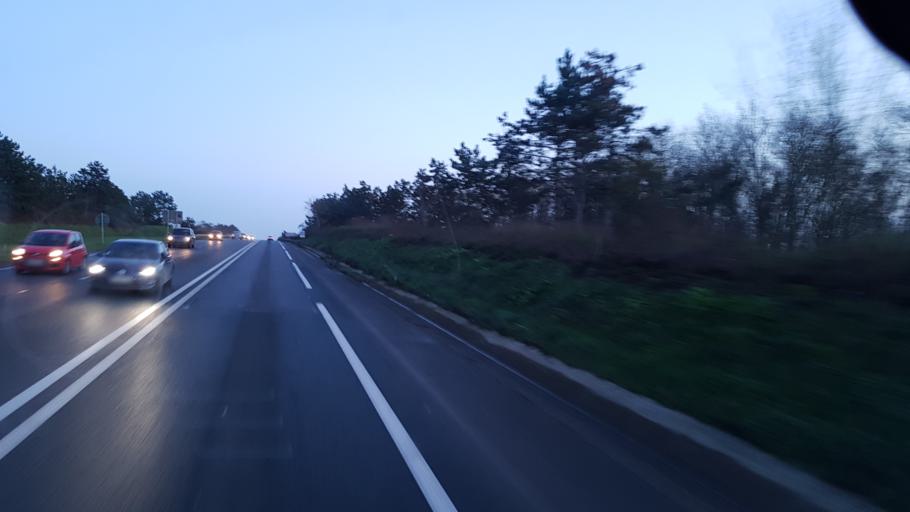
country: FR
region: Nord-Pas-de-Calais
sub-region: Departement du Nord
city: Lambres-lez-Douai
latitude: 50.3504
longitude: 3.0609
